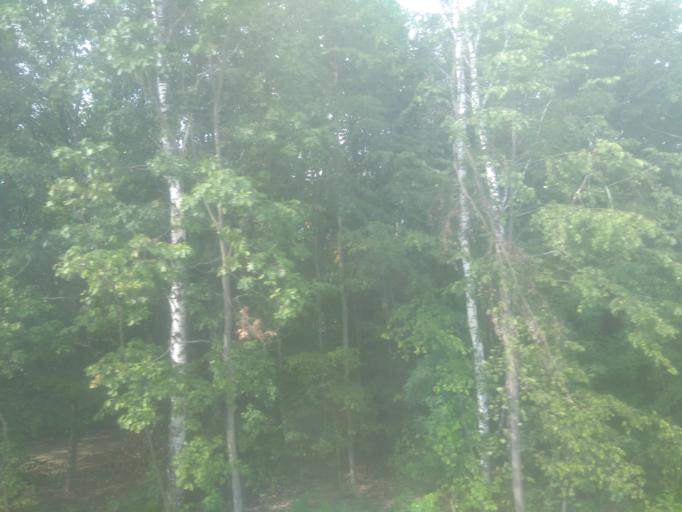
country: CZ
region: Plzensky
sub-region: Okres Plzen-Mesto
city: Pilsen
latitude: 49.7395
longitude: 13.3344
